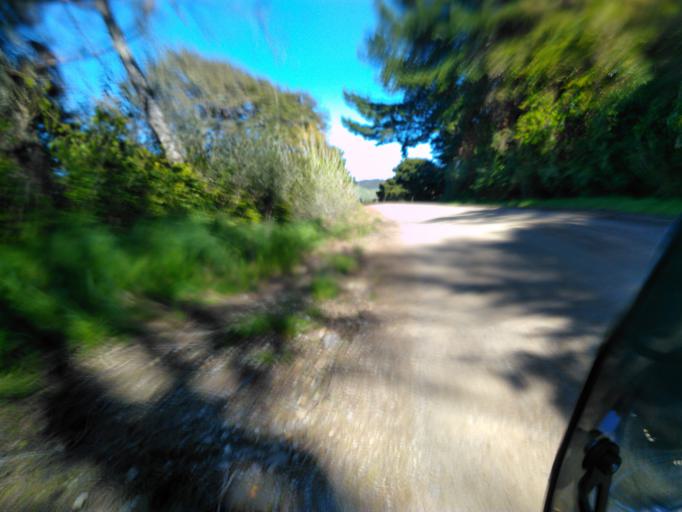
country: NZ
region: Gisborne
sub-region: Gisborne District
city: Gisborne
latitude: -38.4241
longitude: 177.7112
